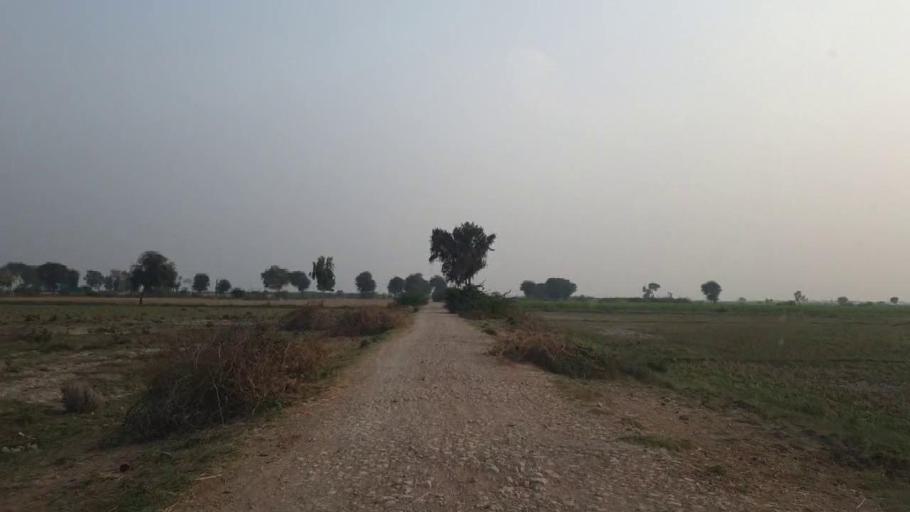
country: PK
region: Sindh
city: Mirpur Batoro
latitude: 24.6540
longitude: 68.3726
